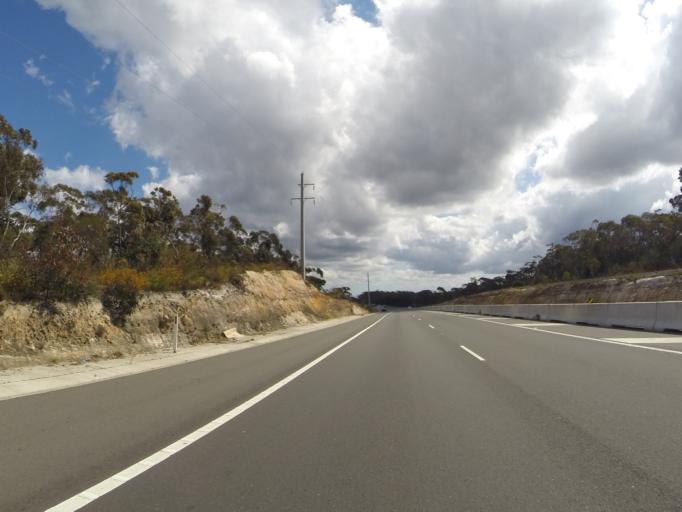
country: AU
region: New South Wales
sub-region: Wollongong
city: Mount Keira
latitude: -34.3587
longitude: 150.8122
